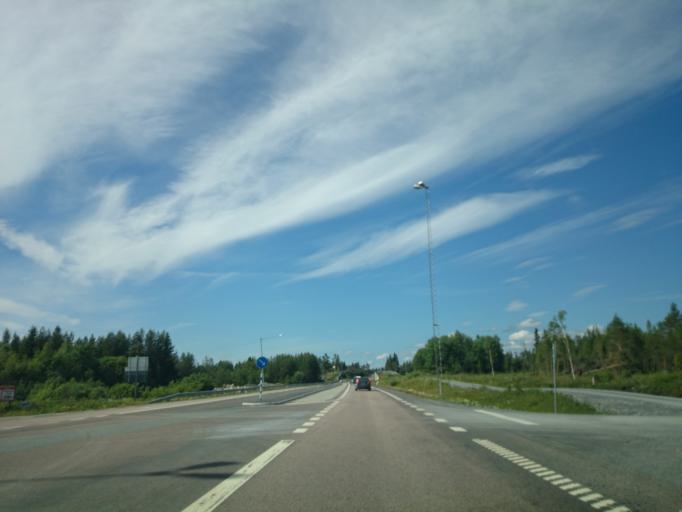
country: SE
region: Jaemtland
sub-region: Krokoms Kommun
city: Krokom
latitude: 63.2863
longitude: 14.5137
